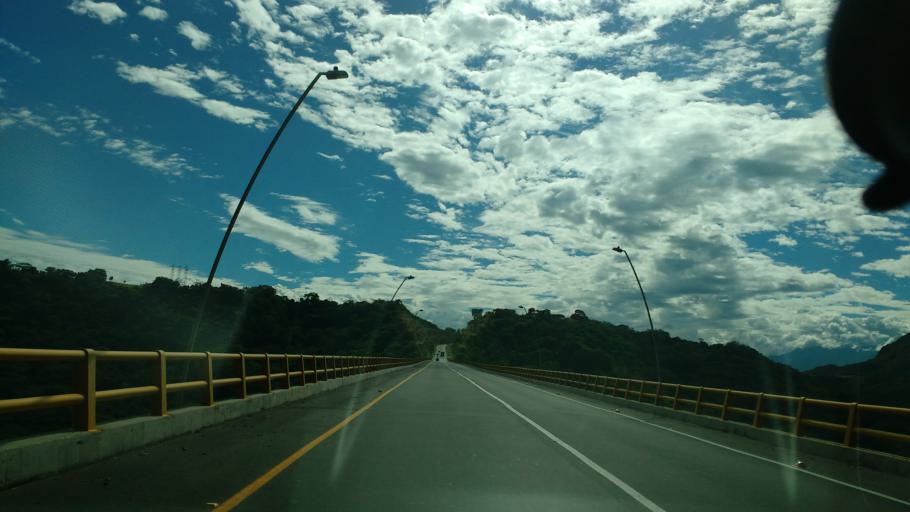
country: CO
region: Tolima
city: Valle de San Juan
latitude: 4.2903
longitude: -75.0321
